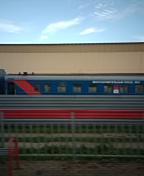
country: RU
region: Moskovskaya
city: Koptevo
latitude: 55.8153
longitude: 37.5237
